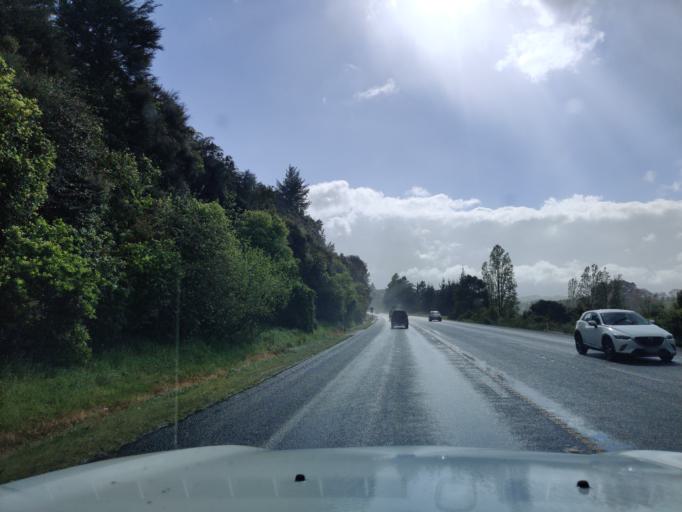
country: NZ
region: Waikato
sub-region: Matamata-Piako District
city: Matamata
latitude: -37.9509
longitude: 175.6337
